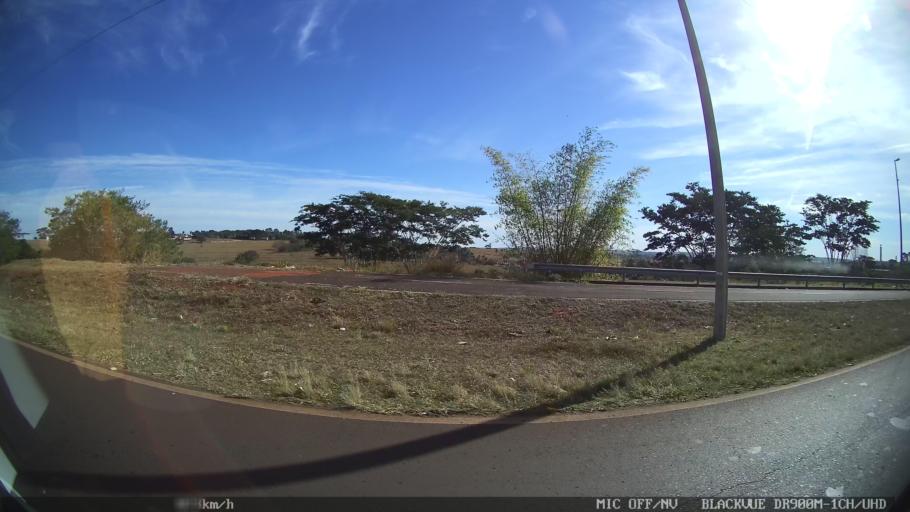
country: BR
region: Sao Paulo
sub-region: Sao Jose Do Rio Preto
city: Sao Jose do Rio Preto
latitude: -20.7368
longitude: -49.3383
